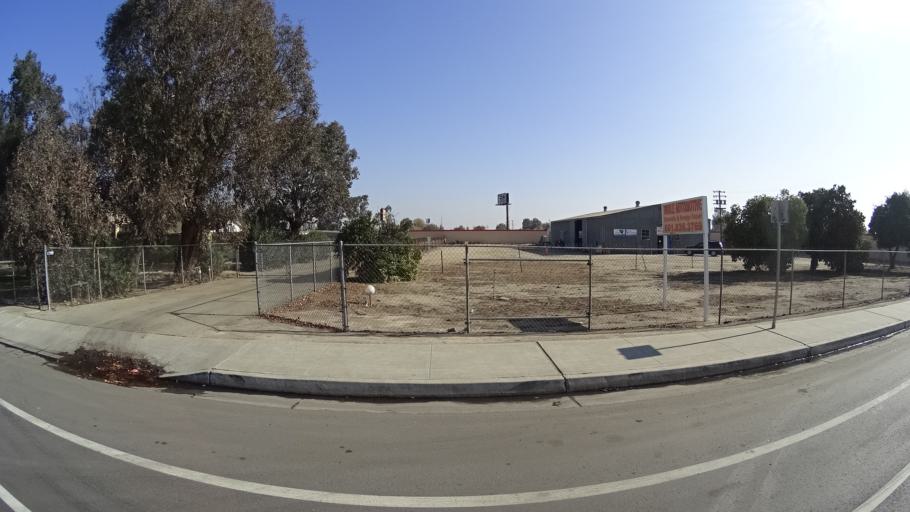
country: US
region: California
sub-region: Kern County
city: Bakersfield
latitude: 35.3198
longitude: -119.0389
